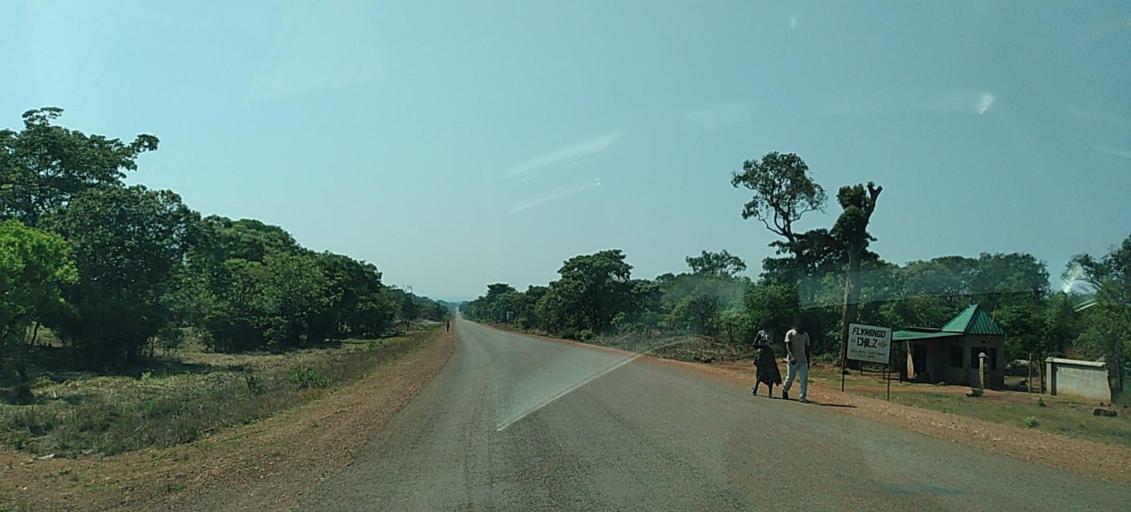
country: ZM
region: North-Western
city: Solwezi
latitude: -12.1180
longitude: 25.5096
